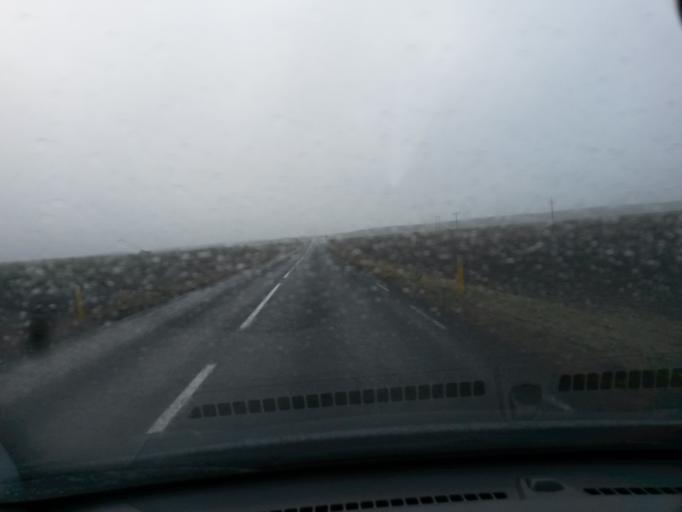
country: IS
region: South
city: Vestmannaeyjar
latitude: 63.4967
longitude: -19.3912
